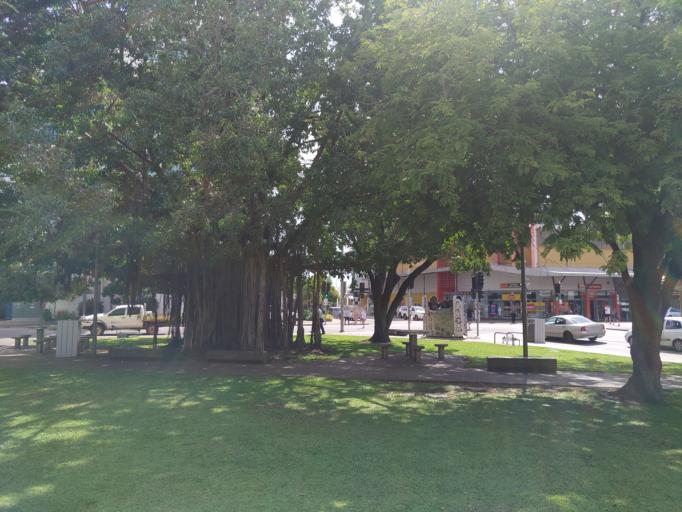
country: AU
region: Northern Territory
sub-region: Darwin
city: Darwin
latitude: -12.4635
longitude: 130.8414
